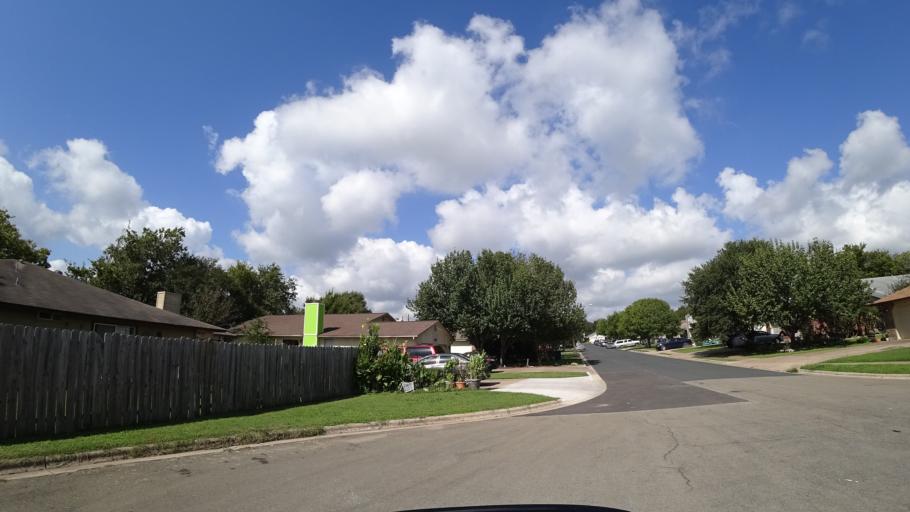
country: US
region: Texas
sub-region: Travis County
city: Shady Hollow
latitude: 30.1998
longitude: -97.8092
